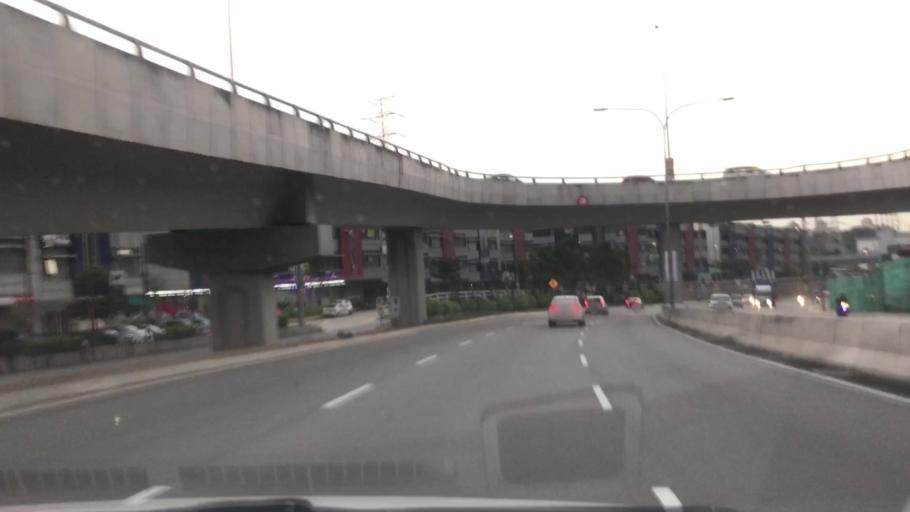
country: MY
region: Selangor
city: Kampong Baharu Balakong
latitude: 3.0490
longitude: 101.6712
